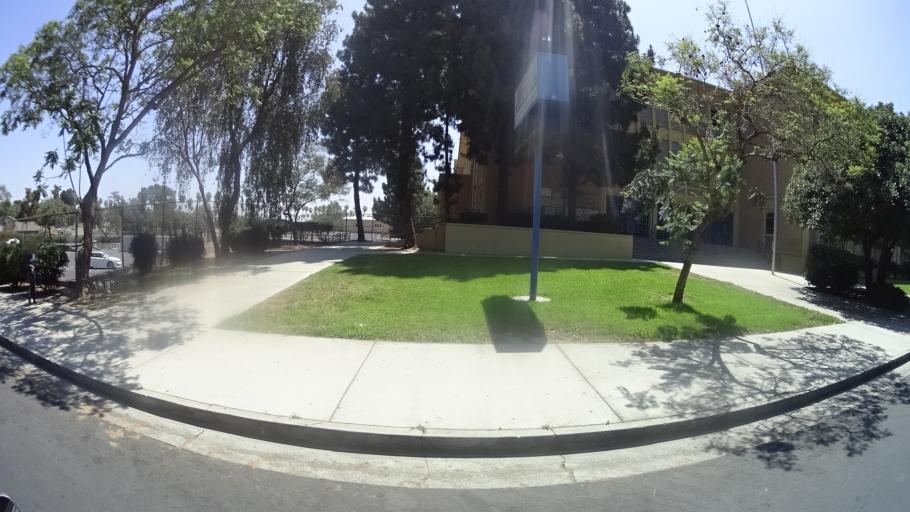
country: US
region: California
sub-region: Los Angeles County
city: View Park-Windsor Hills
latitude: 33.9974
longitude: -118.3294
